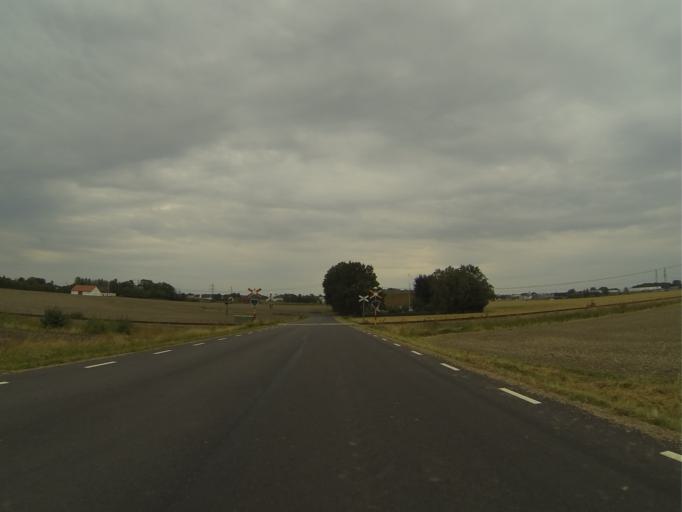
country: SE
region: Skane
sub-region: Burlovs Kommun
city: Arloev
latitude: 55.6251
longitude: 13.1156
